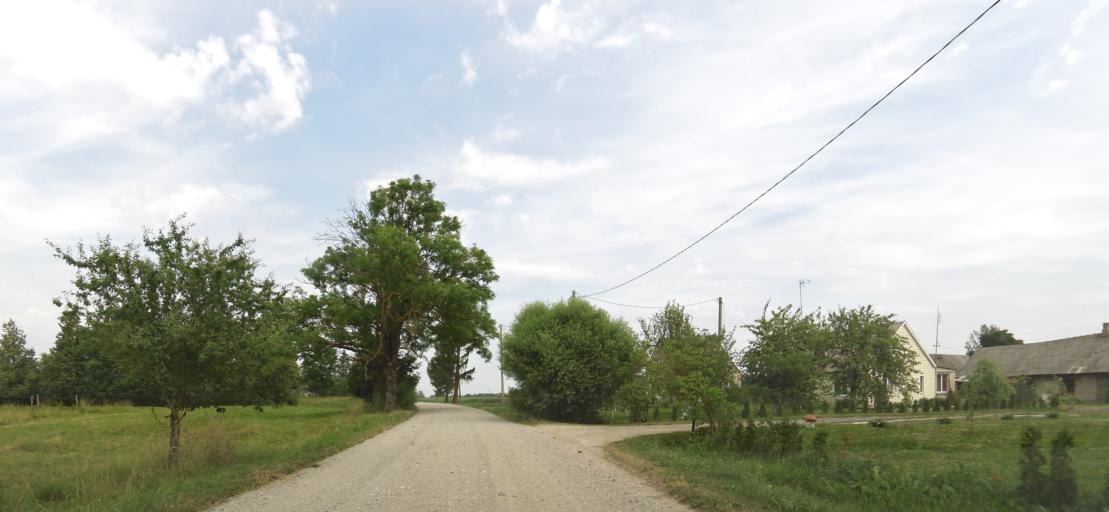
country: LT
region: Panevezys
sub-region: Birzai
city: Birzai
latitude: 56.3494
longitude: 24.7467
